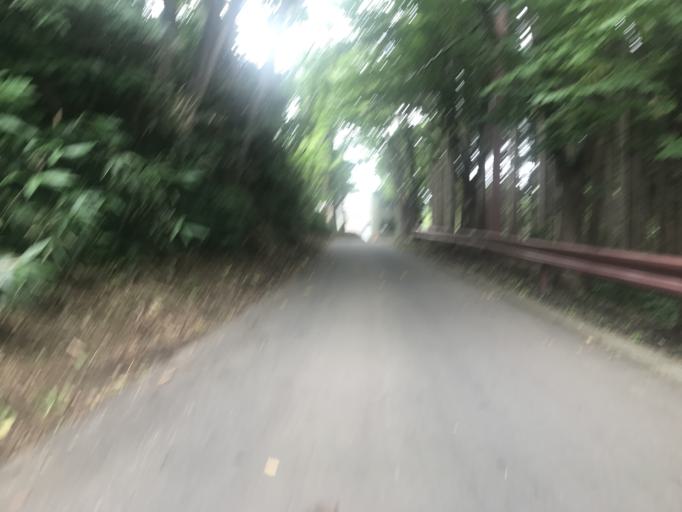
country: JP
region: Hokkaido
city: Kamiiso
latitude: 41.4330
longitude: 140.1090
